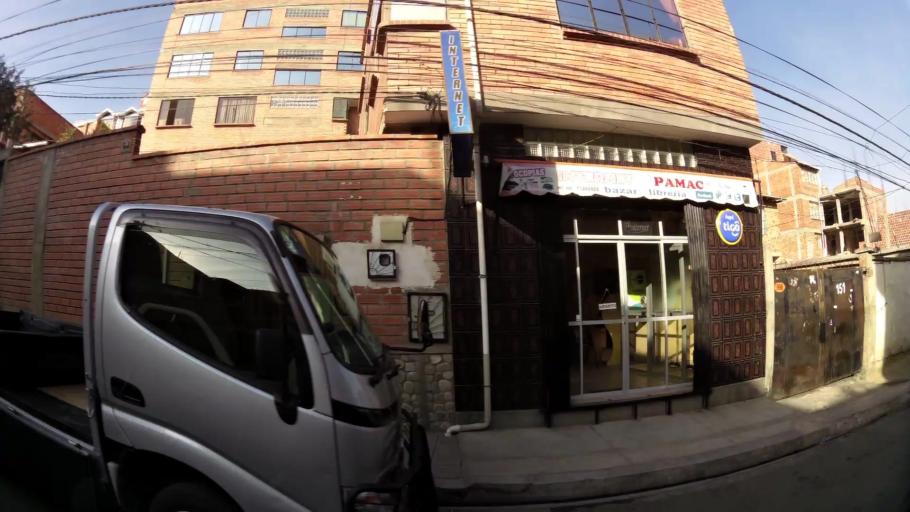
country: BO
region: La Paz
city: La Paz
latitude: -16.5278
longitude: -68.0954
